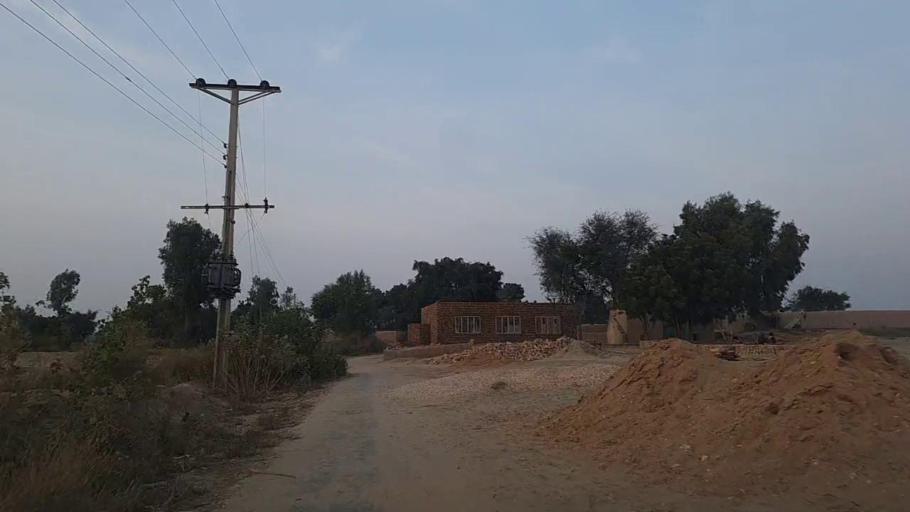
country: PK
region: Sindh
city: Jam Sahib
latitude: 26.4756
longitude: 68.5483
